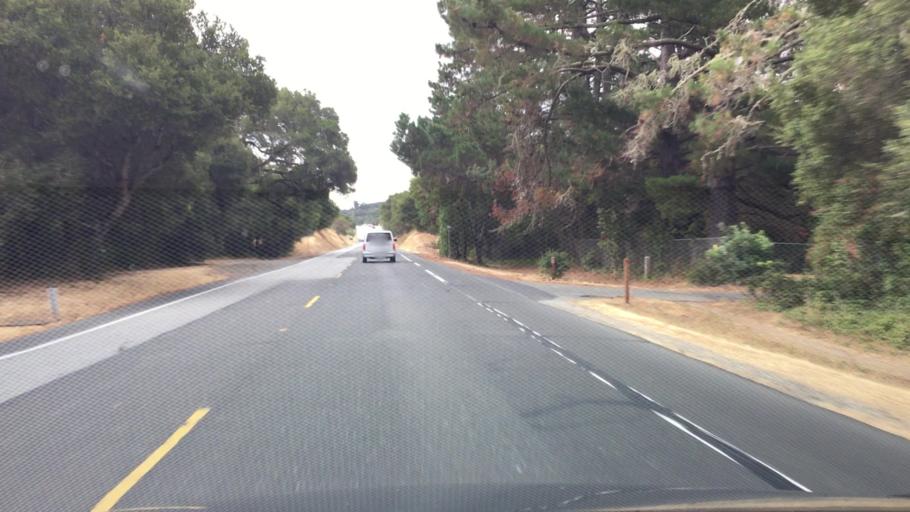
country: US
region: California
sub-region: San Mateo County
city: Emerald Lake Hills
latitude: 37.4687
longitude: -122.3024
